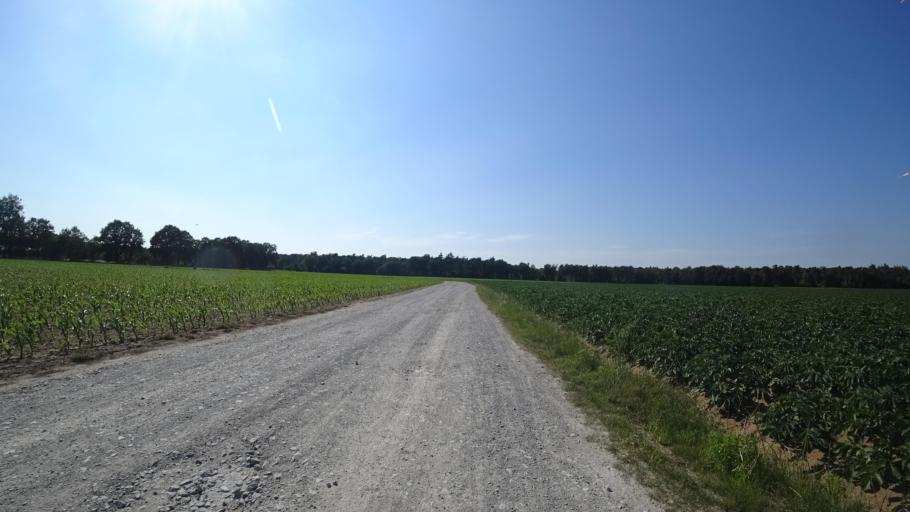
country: DE
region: North Rhine-Westphalia
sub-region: Regierungsbezirk Detmold
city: Rheda-Wiedenbruck
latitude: 51.8859
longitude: 8.3271
